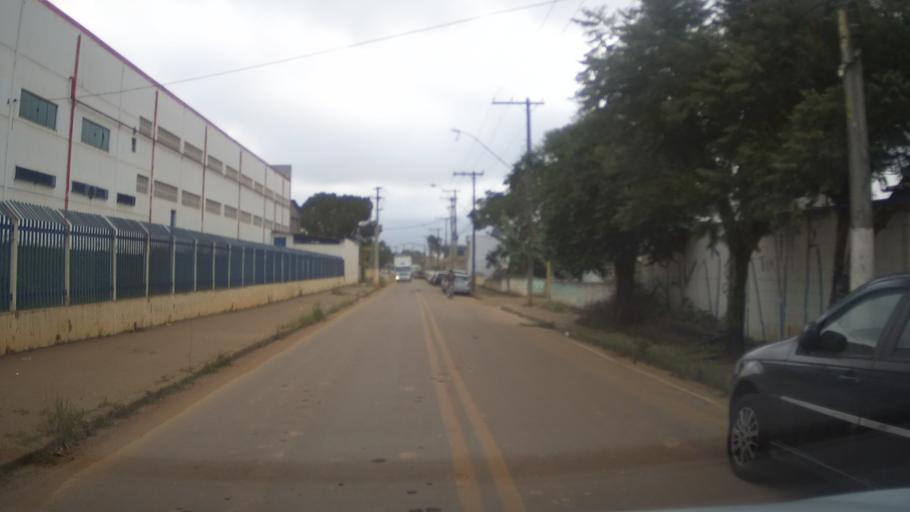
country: BR
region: Sao Paulo
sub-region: Aruja
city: Aruja
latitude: -23.4078
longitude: -46.3613
